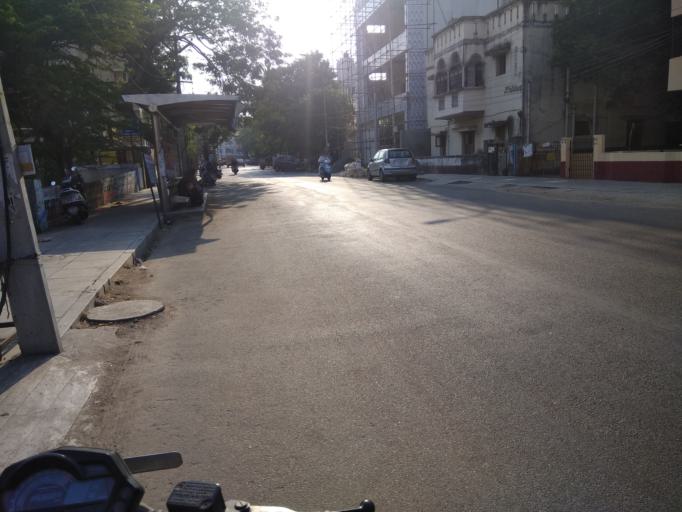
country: IN
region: Tamil Nadu
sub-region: Kancheepuram
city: Madipakkam
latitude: 12.9807
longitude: 80.1873
